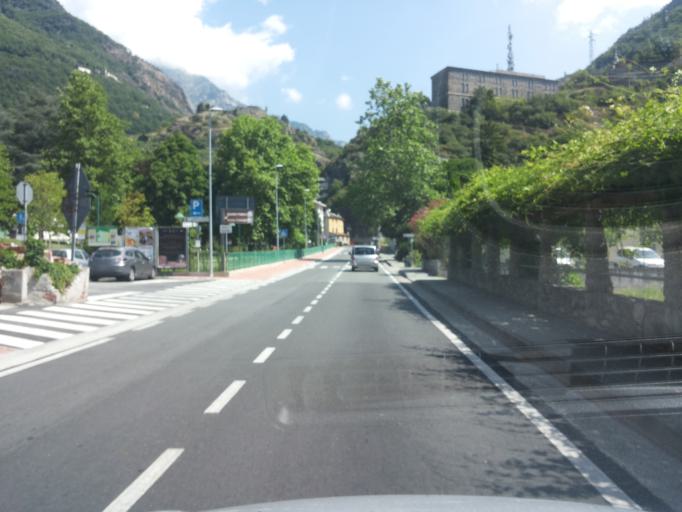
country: IT
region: Aosta Valley
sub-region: Valle d'Aosta
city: Pont-Saint-Martin
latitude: 45.5966
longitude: 7.7988
